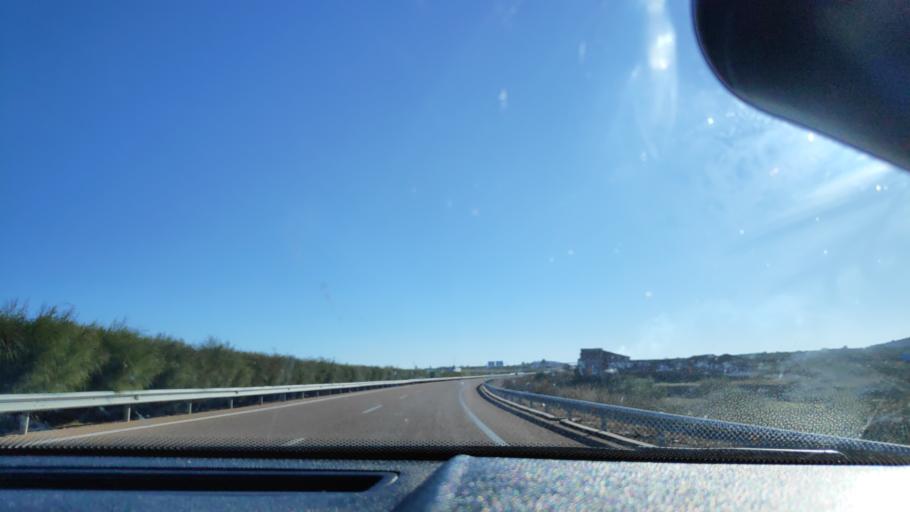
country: ES
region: Extremadura
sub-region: Provincia de Badajoz
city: Villafranca de los Barros
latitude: 38.5247
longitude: -6.3497
